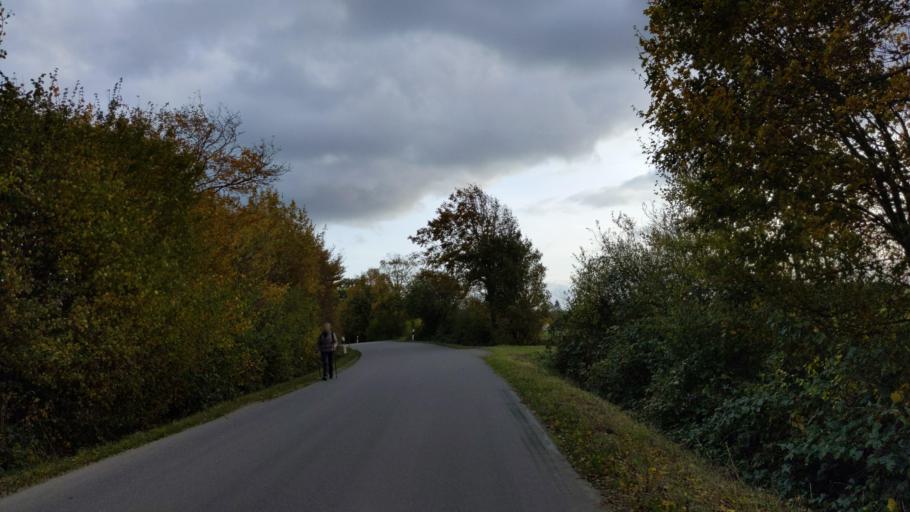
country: DE
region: Schleswig-Holstein
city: Kasseedorf
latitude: 54.1247
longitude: 10.7082
